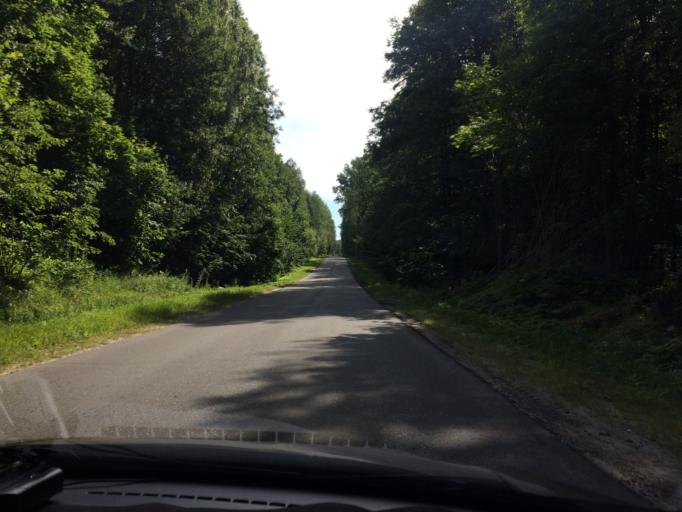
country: RU
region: Mariy-El
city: Surok
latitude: 56.5711
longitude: 48.1463
